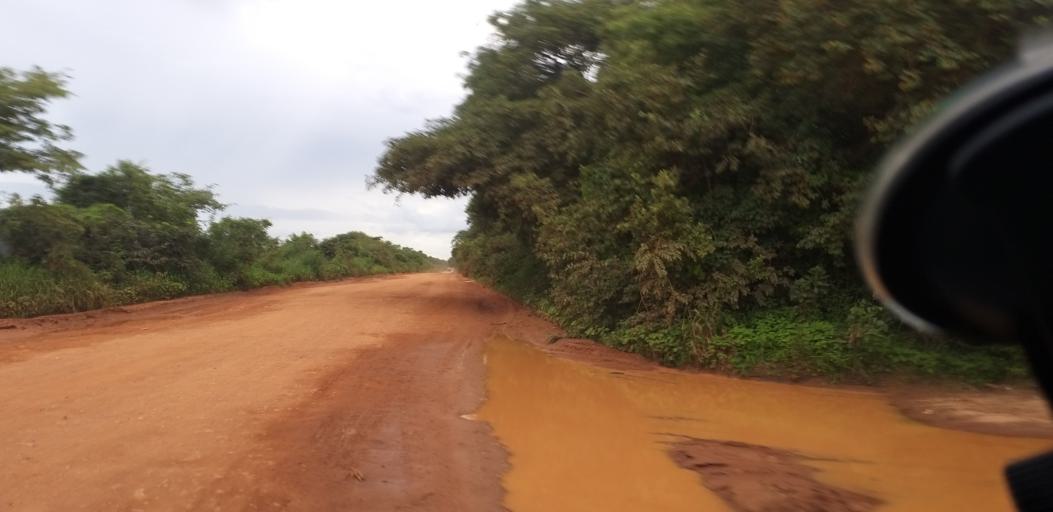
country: ZM
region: Lusaka
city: Lusaka
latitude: -15.2089
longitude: 28.4356
